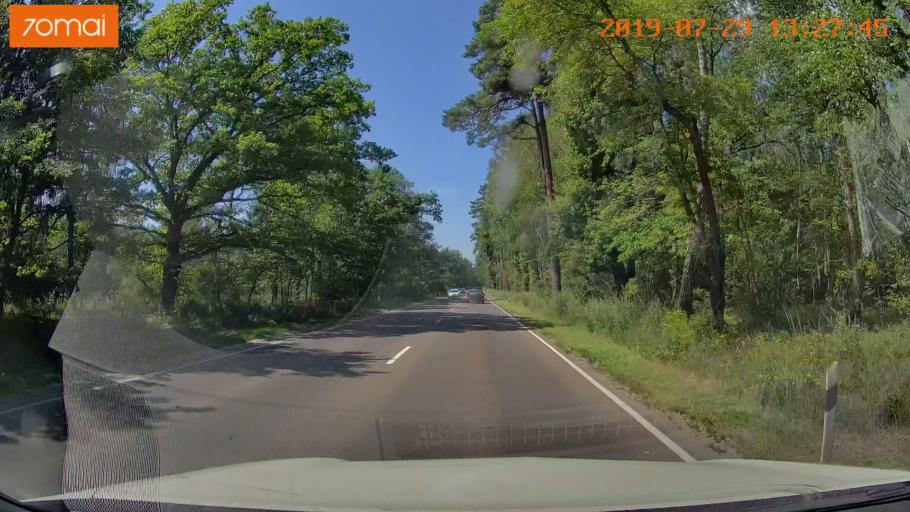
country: RU
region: Kaliningrad
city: Vzmorye
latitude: 54.7047
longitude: 20.2942
